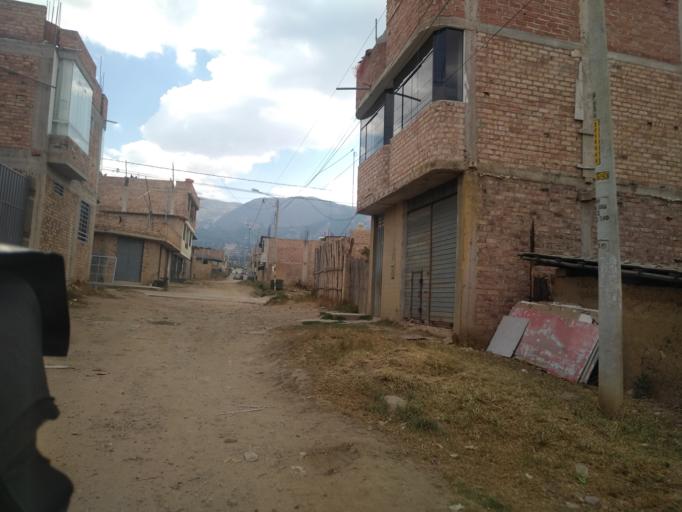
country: PE
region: Cajamarca
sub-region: Provincia de Cajamarca
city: Cajamarca
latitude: -7.1771
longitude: -78.4922
